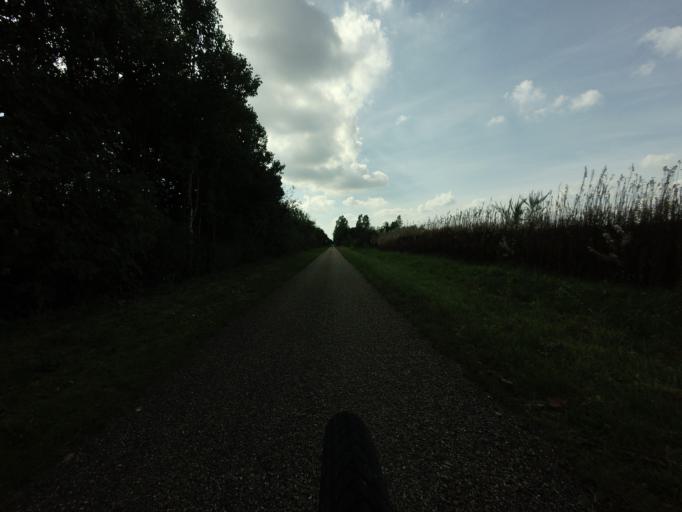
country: DK
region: Central Jutland
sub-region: Herning Kommune
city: Sunds
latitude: 56.2282
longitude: 9.0749
